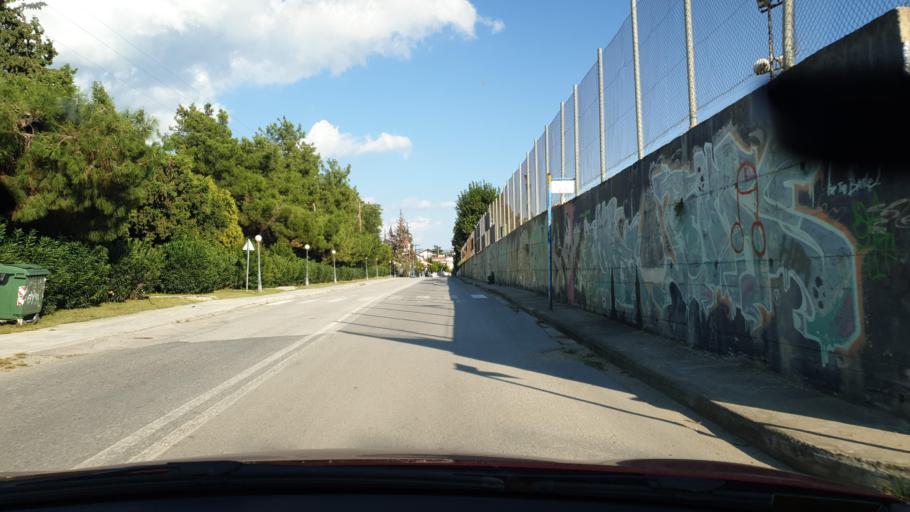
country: GR
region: Central Macedonia
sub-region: Nomos Thessalonikis
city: Souroti
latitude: 40.4741
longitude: 23.0880
